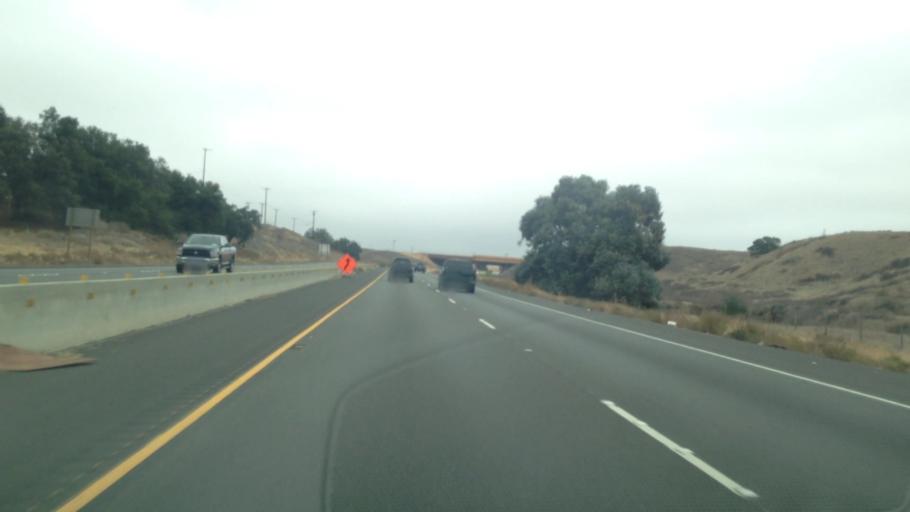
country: US
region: California
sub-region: Riverside County
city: Beaumont
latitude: 33.9329
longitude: -117.0230
